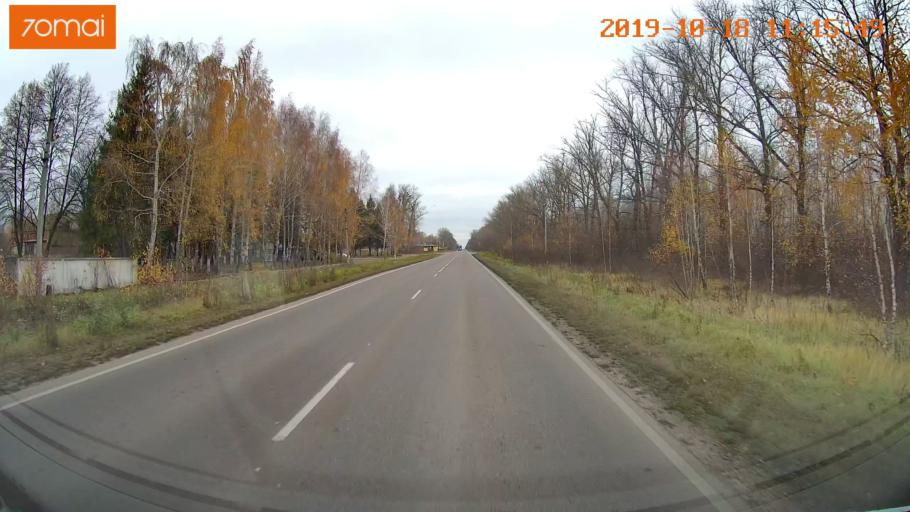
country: RU
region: Tula
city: Kimovsk
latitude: 53.9978
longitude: 38.5479
